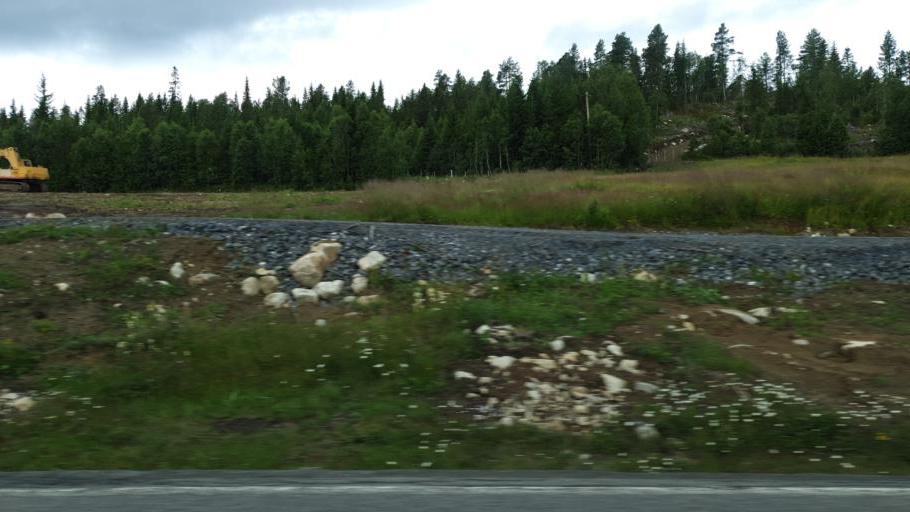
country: NO
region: Sor-Trondelag
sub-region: Rennebu
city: Berkak
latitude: 62.8566
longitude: 10.0213
